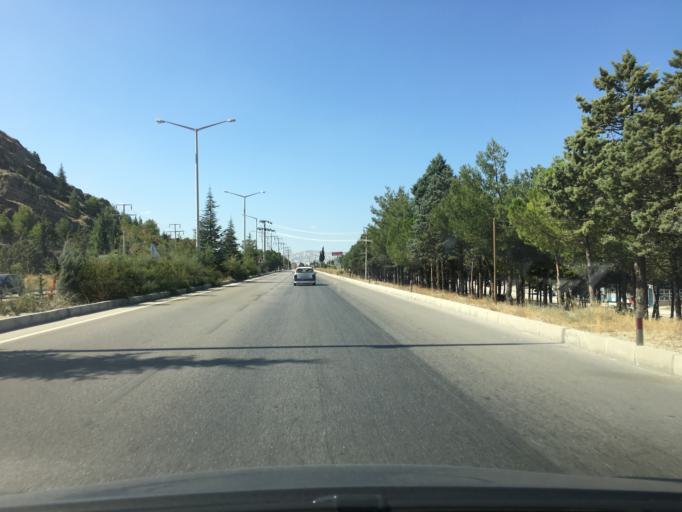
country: TR
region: Burdur
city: Burdur
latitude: 37.7453
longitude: 30.3177
